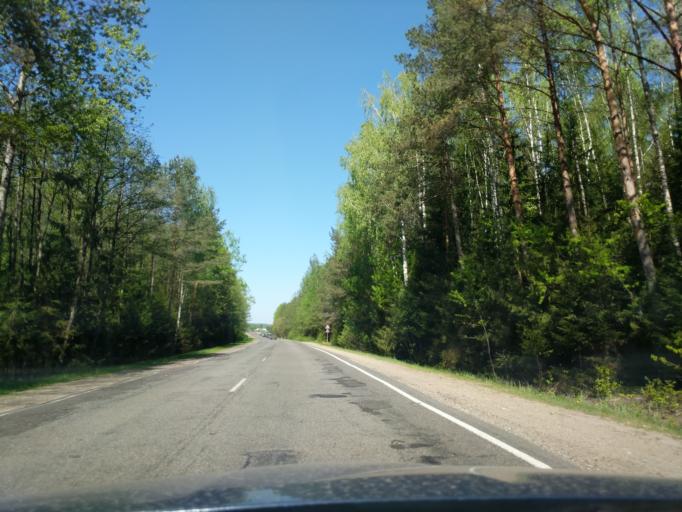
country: BY
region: Minsk
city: Il'ya
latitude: 54.4082
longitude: 27.3118
